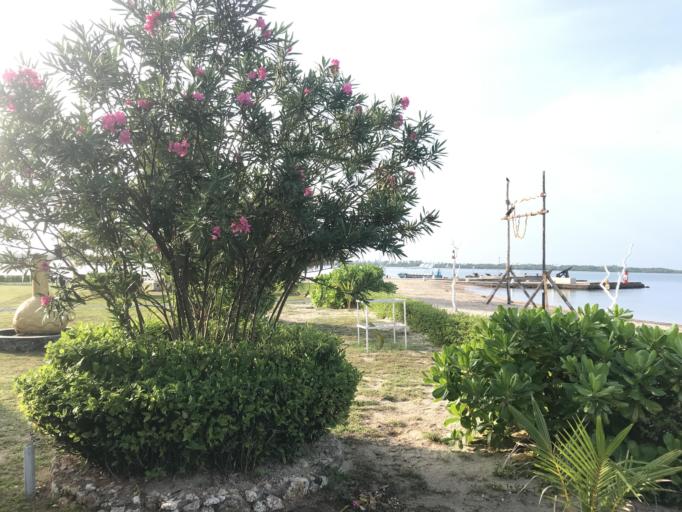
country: LK
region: Northern Province
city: Jaffna
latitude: 9.7136
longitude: 79.8505
